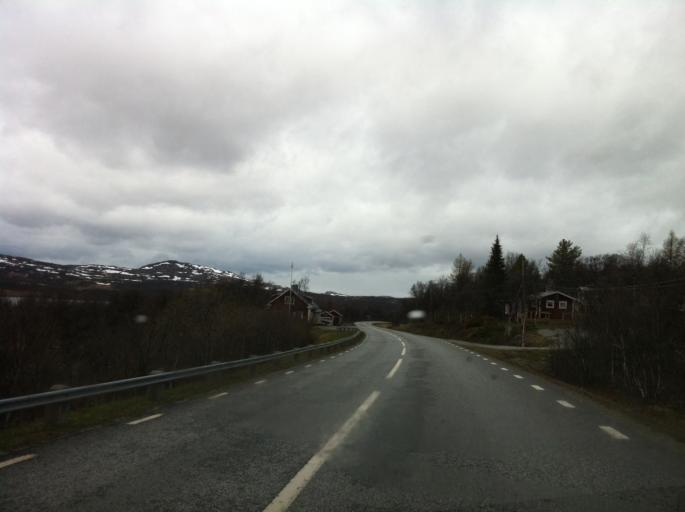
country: NO
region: Sor-Trondelag
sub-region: Tydal
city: Aas
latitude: 62.6067
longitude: 12.1632
